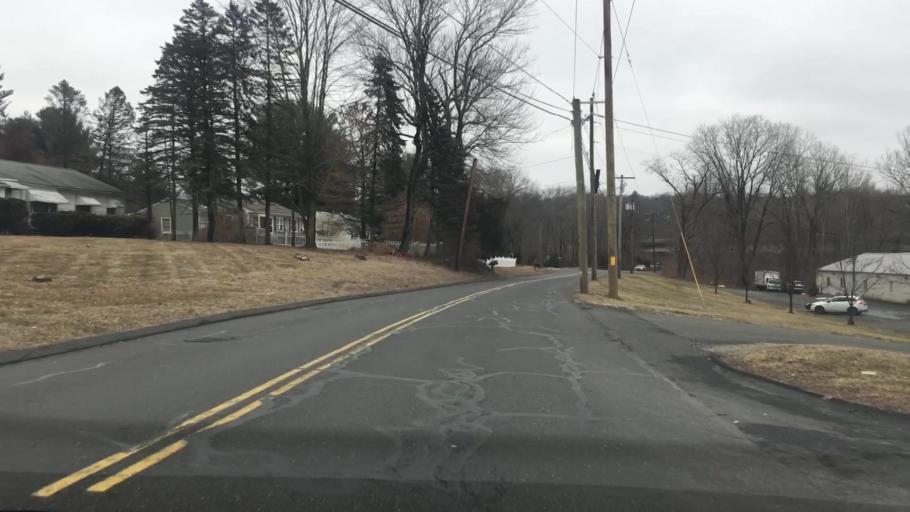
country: US
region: Connecticut
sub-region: Fairfield County
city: Danbury
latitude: 41.4394
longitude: -73.4029
